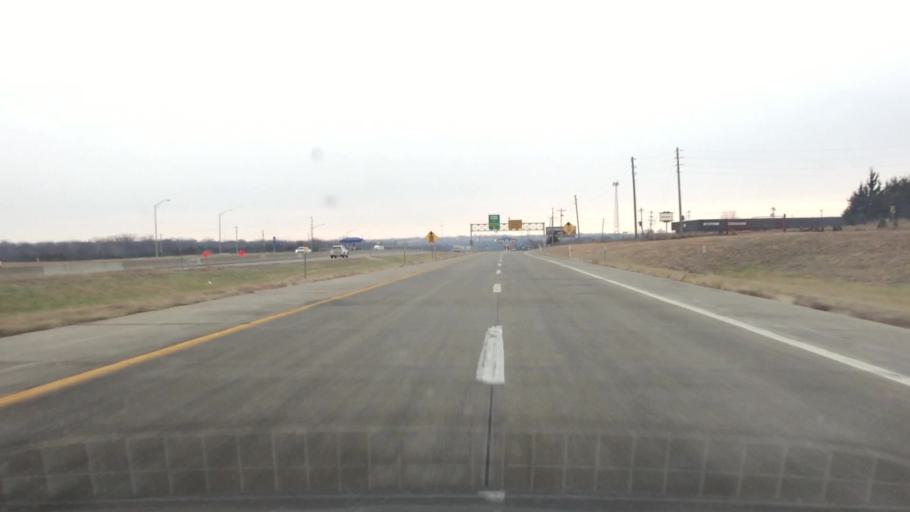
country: US
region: Kansas
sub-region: Shawnee County
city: Topeka
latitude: 39.0309
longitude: -95.6142
